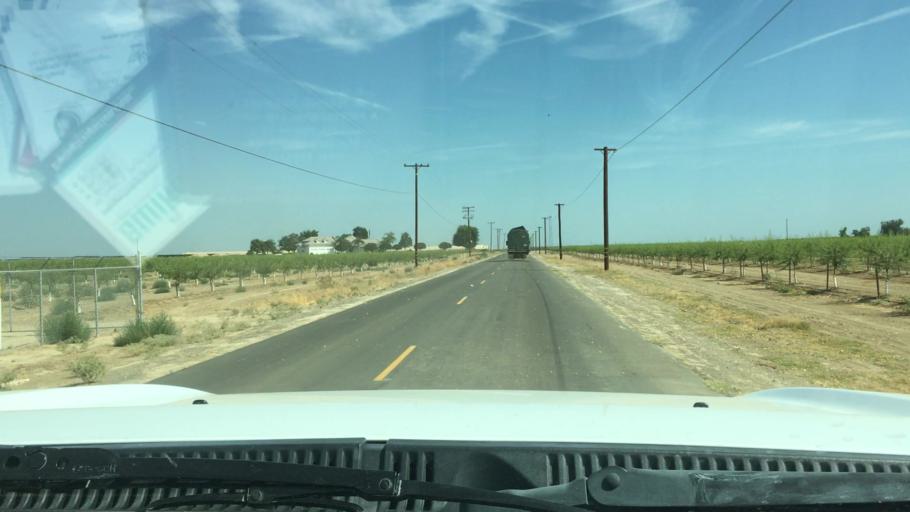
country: US
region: California
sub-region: Kern County
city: Shafter
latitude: 35.4602
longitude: -119.3681
